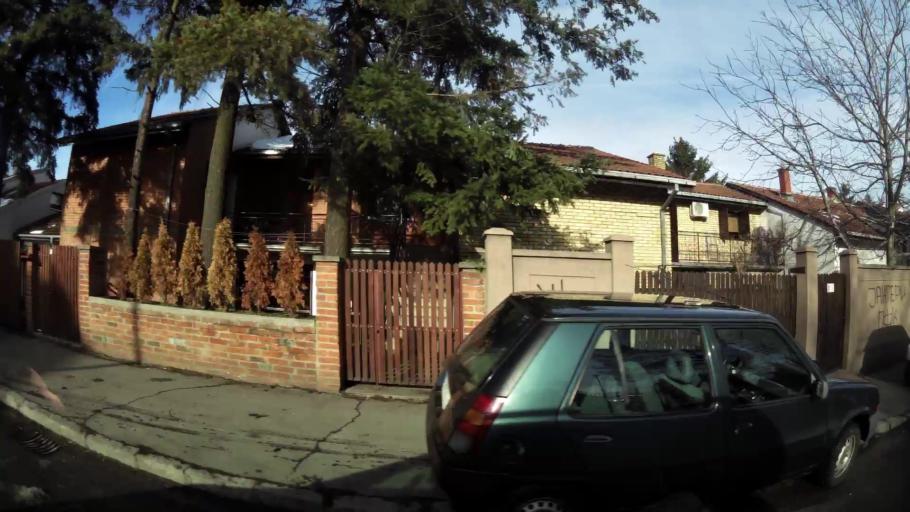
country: RS
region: Central Serbia
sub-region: Belgrade
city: Rakovica
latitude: 44.7209
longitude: 20.4223
